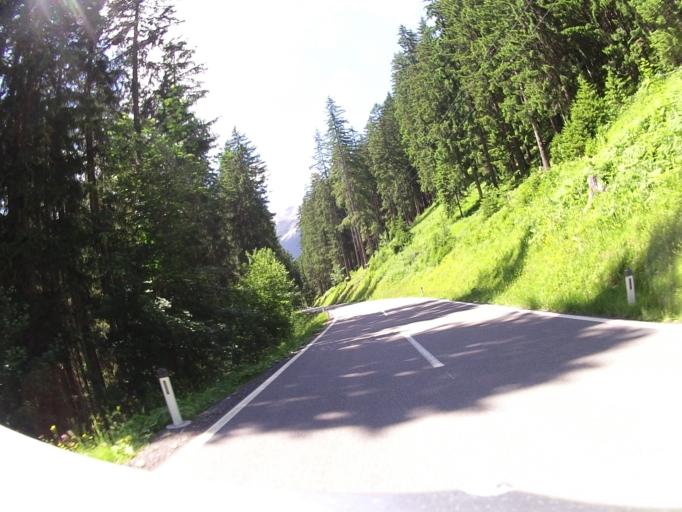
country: AT
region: Tyrol
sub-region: Politischer Bezirk Reutte
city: Elmen
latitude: 47.3157
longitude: 10.5607
